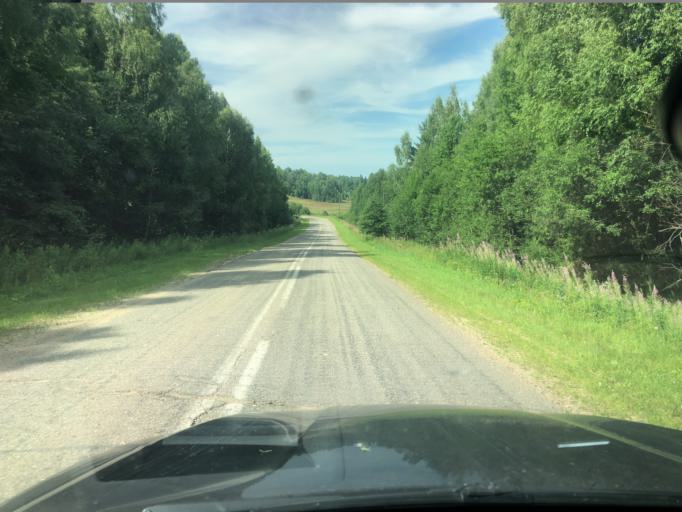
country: RU
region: Jaroslavl
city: Pereslavl'-Zalesskiy
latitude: 57.0338
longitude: 38.9088
